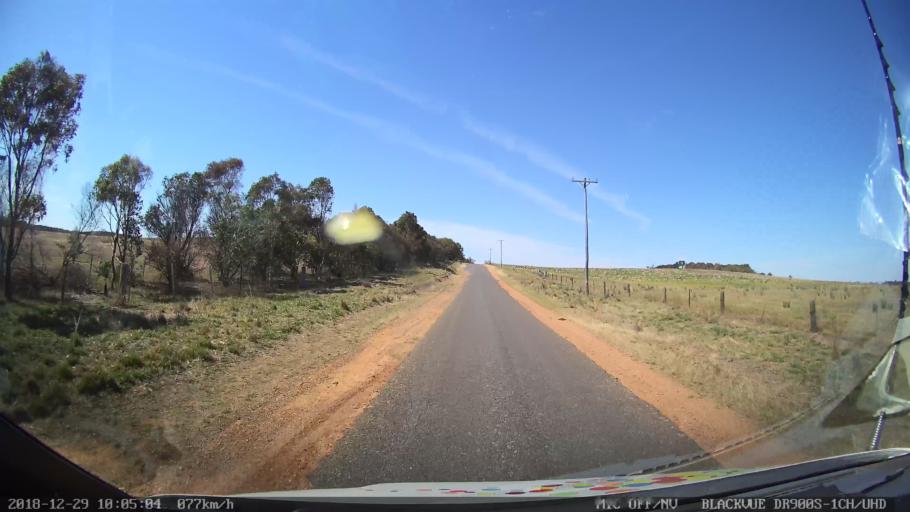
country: AU
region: New South Wales
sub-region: Goulburn Mulwaree
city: Goulburn
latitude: -34.8293
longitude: 149.4539
